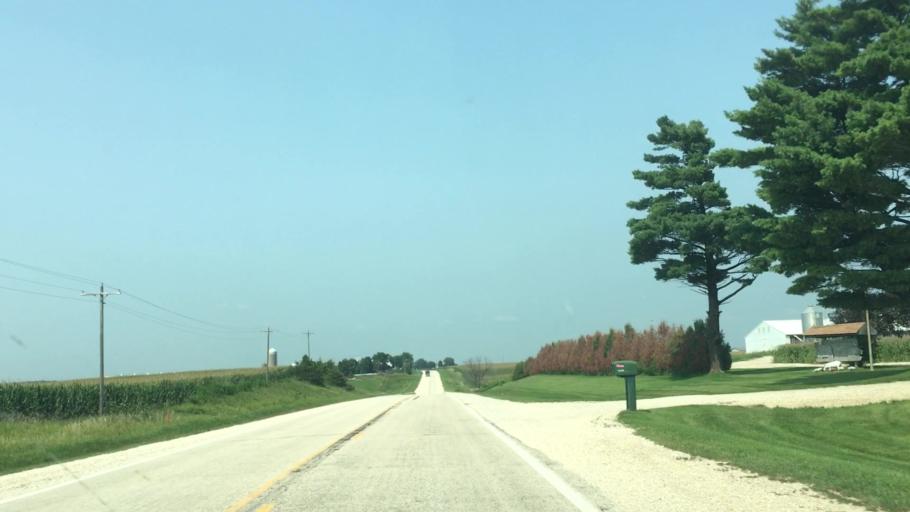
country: US
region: Iowa
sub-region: Fayette County
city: West Union
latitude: 43.0084
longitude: -91.8243
